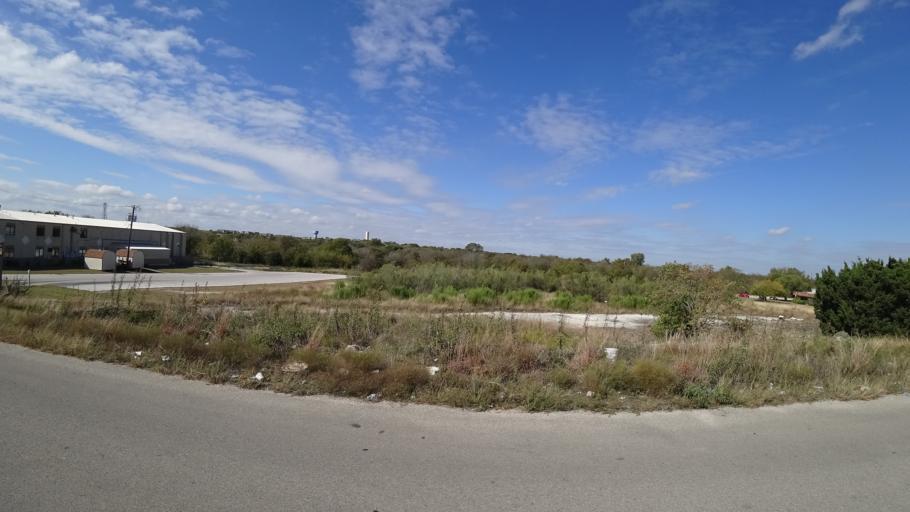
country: US
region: Texas
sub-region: Travis County
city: Windemere
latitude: 30.4482
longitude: -97.6413
